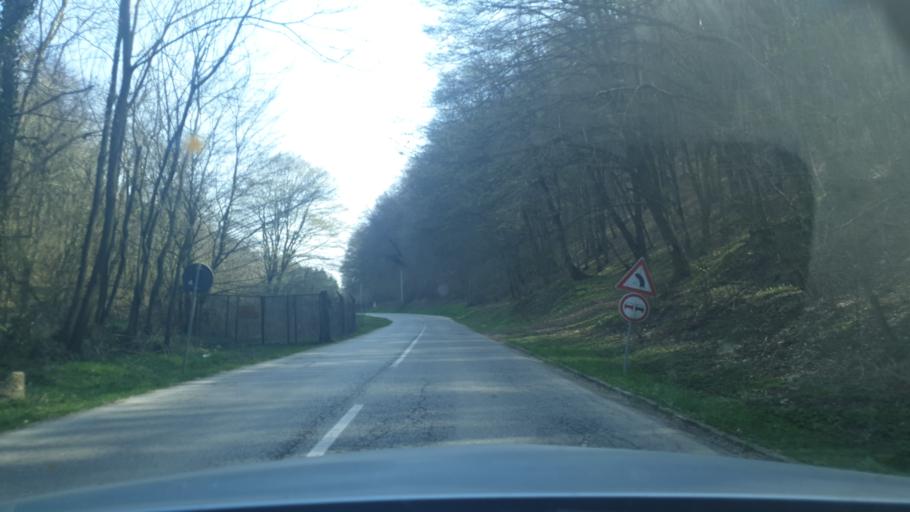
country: RS
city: Vrdnik
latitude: 45.1381
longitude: 19.7756
